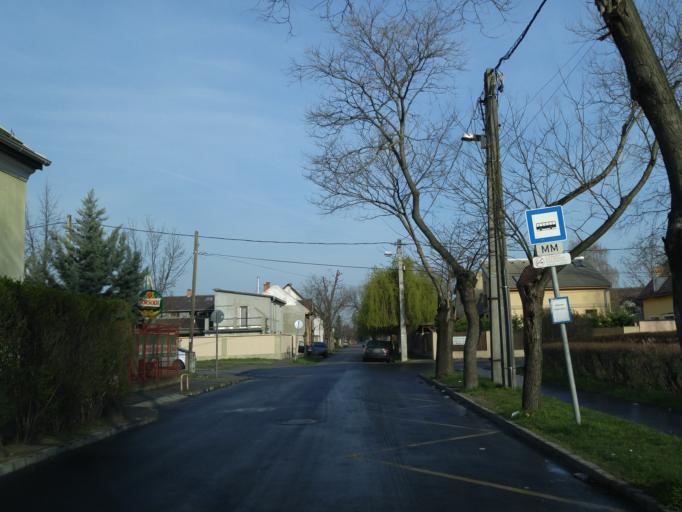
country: HU
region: Budapest
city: Budapest XX. keruelet
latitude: 47.4327
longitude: 19.1268
